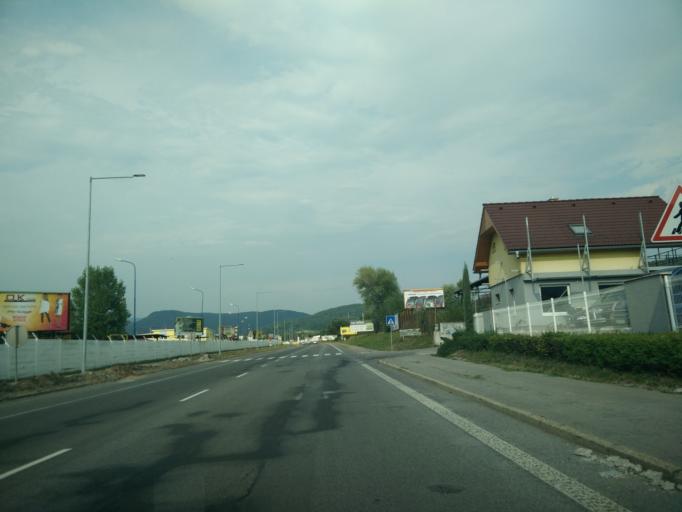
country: SK
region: Banskobystricky
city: Ziar nad Hronom
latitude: 48.5666
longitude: 18.8595
